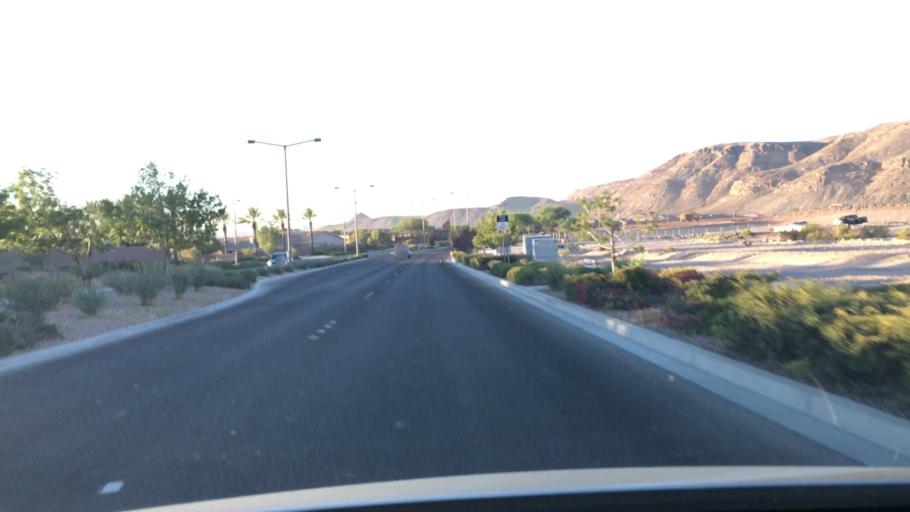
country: US
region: Nevada
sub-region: Clark County
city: Summerlin South
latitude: 36.0954
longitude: -115.3251
